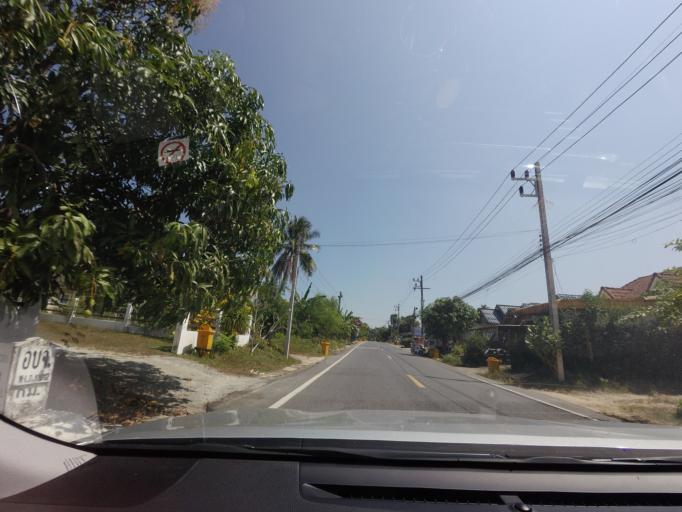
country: TH
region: Phangnga
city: Takua Thung
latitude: 8.2532
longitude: 98.4129
